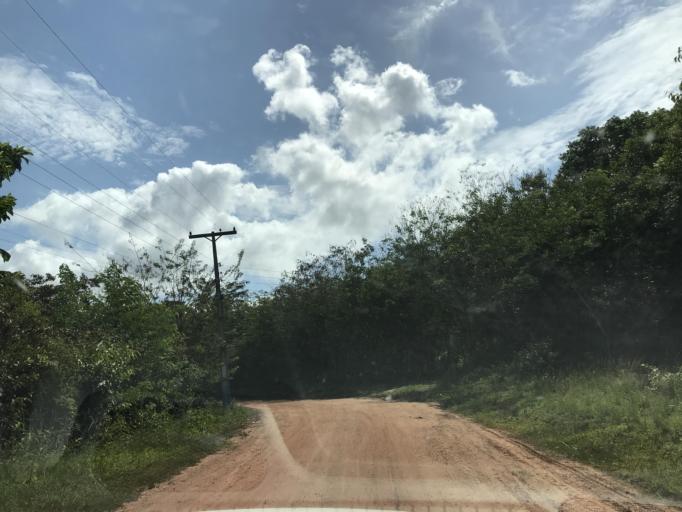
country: BR
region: Bahia
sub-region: Entre Rios
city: Entre Rios
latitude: -12.1877
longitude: -38.0486
